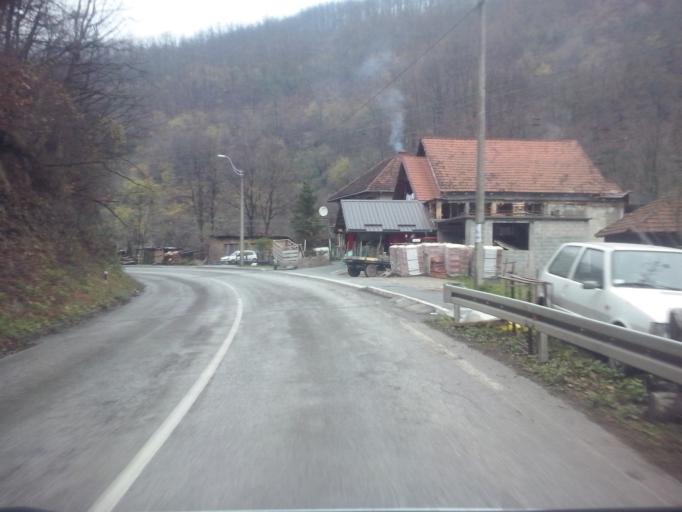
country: RS
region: Central Serbia
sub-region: Moravicki Okrug
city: Ivanjica
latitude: 43.5595
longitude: 20.2574
